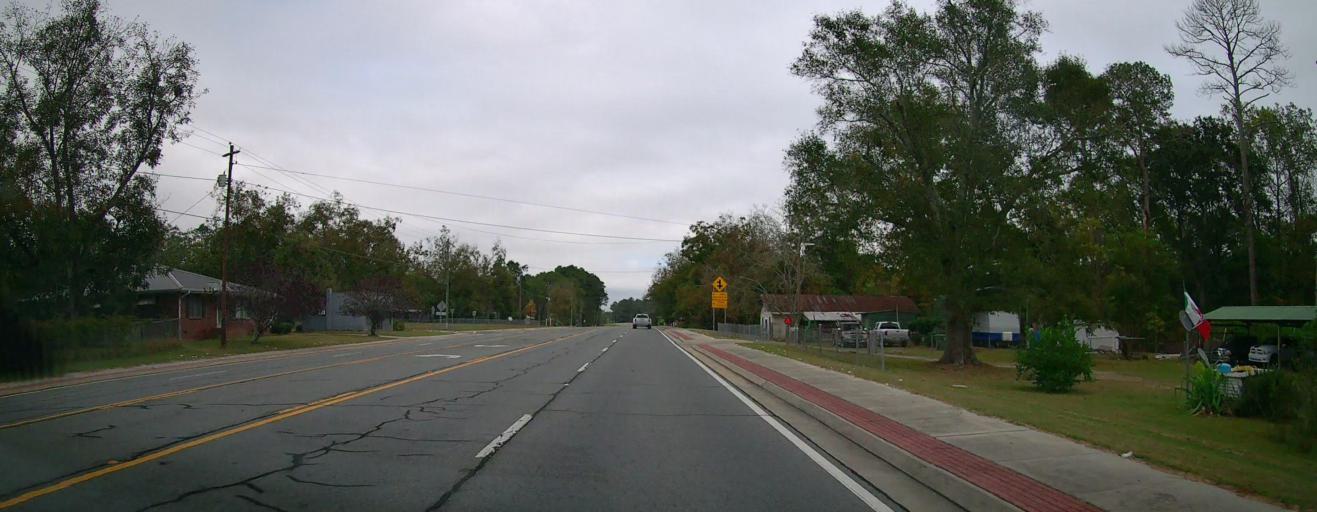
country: US
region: Georgia
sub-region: Tift County
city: Omega
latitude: 31.3037
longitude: -83.6447
